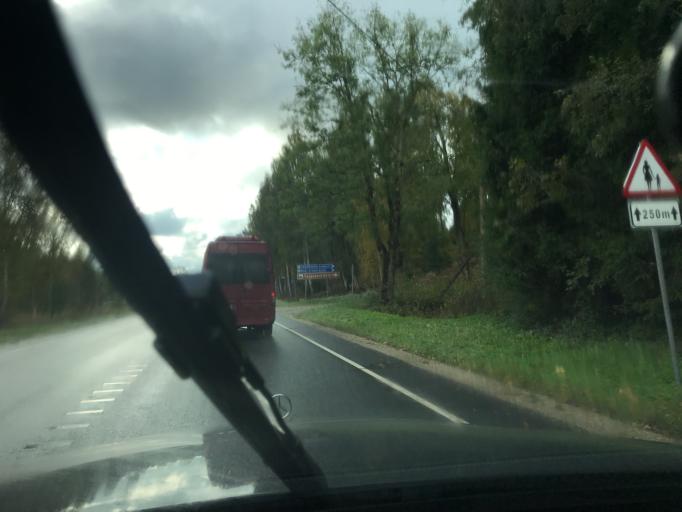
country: EE
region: Viljandimaa
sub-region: Karksi vald
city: Karksi-Nuia
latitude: 58.0149
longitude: 25.6862
